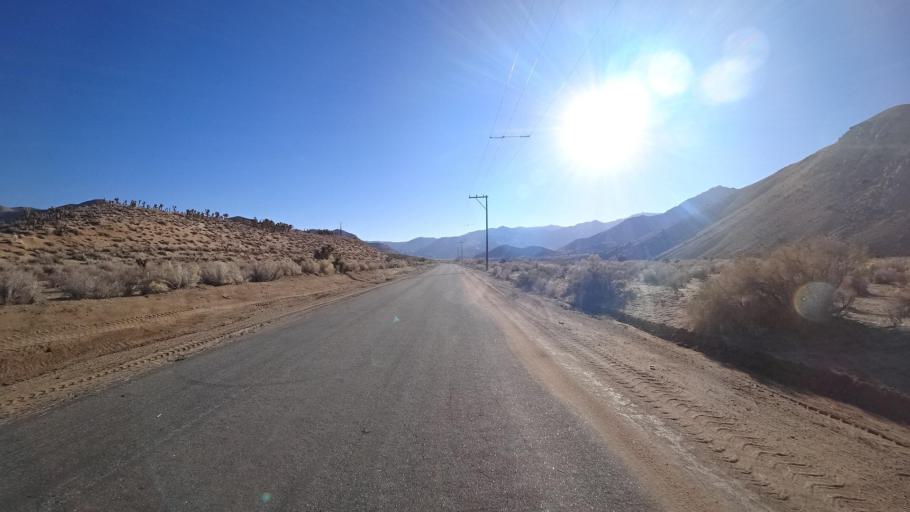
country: US
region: California
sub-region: Kern County
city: Weldon
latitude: 35.6095
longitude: -118.2436
